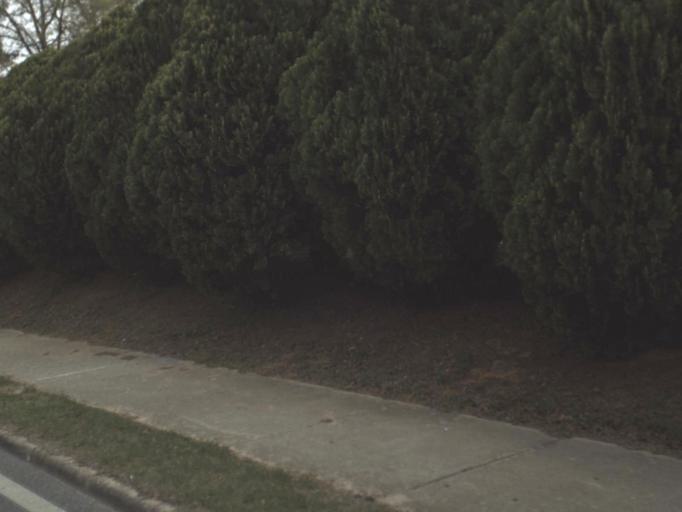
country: US
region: Florida
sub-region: Holmes County
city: Bonifay
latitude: 30.7994
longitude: -85.6794
